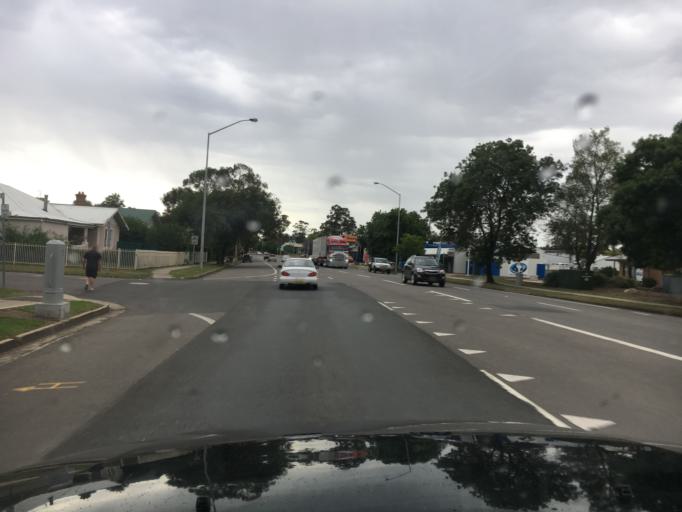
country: AU
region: New South Wales
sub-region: Muswellbrook
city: Muswellbrook
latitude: -32.2710
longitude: 150.8894
